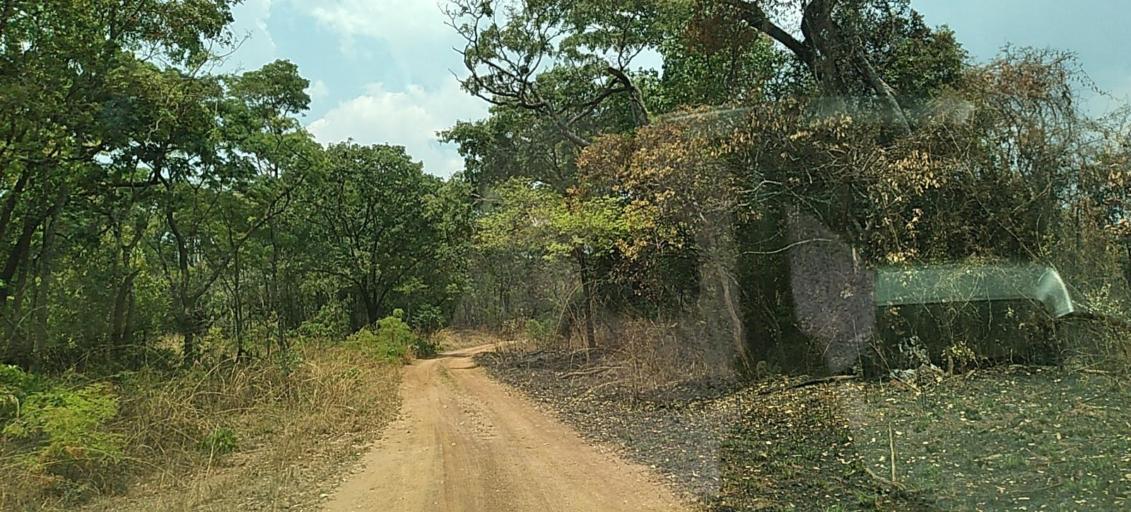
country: ZM
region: Copperbelt
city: Chingola
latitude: -12.7894
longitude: 27.6514
